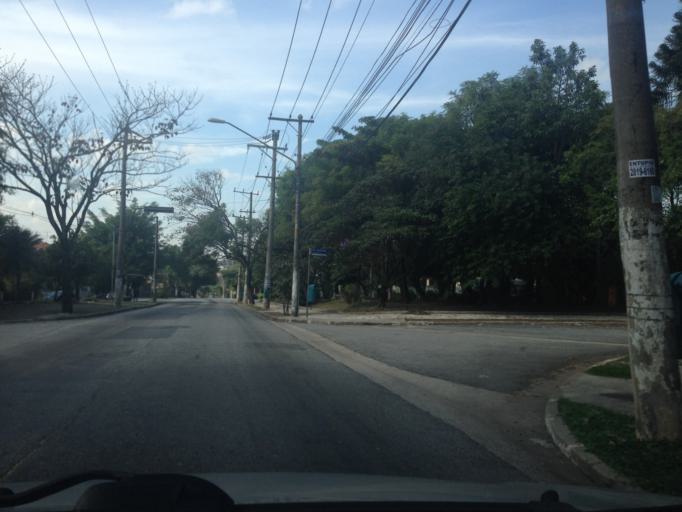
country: BR
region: Sao Paulo
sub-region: Osasco
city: Osasco
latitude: -23.5215
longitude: -46.7153
